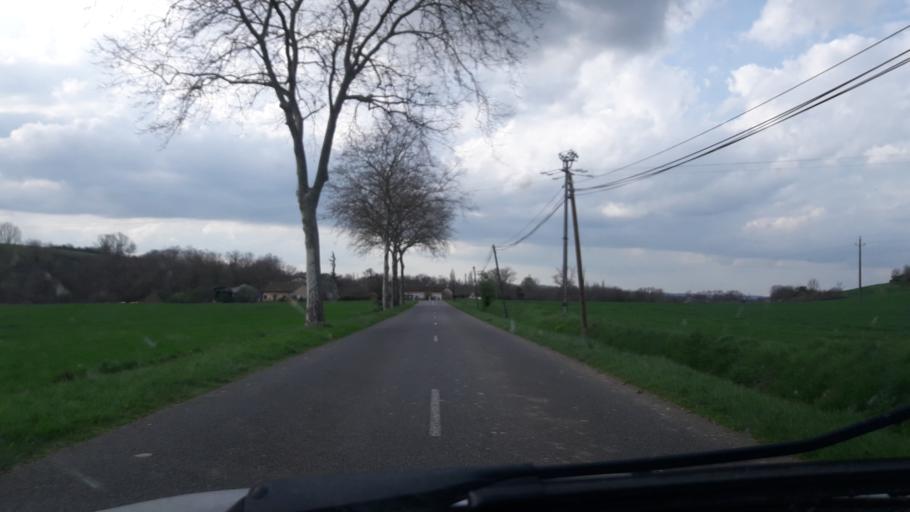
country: FR
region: Midi-Pyrenees
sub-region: Departement de la Haute-Garonne
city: Rieux-Volvestre
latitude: 43.2621
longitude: 1.2224
